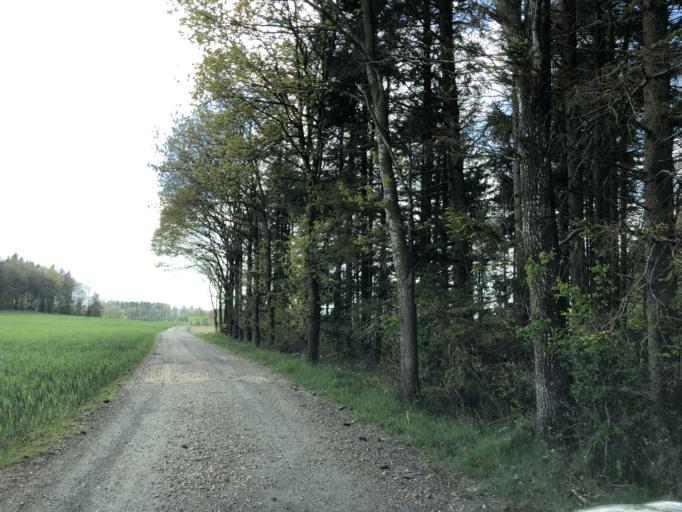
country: DK
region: Central Jutland
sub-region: Herning Kommune
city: Avlum
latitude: 56.2970
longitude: 8.7507
